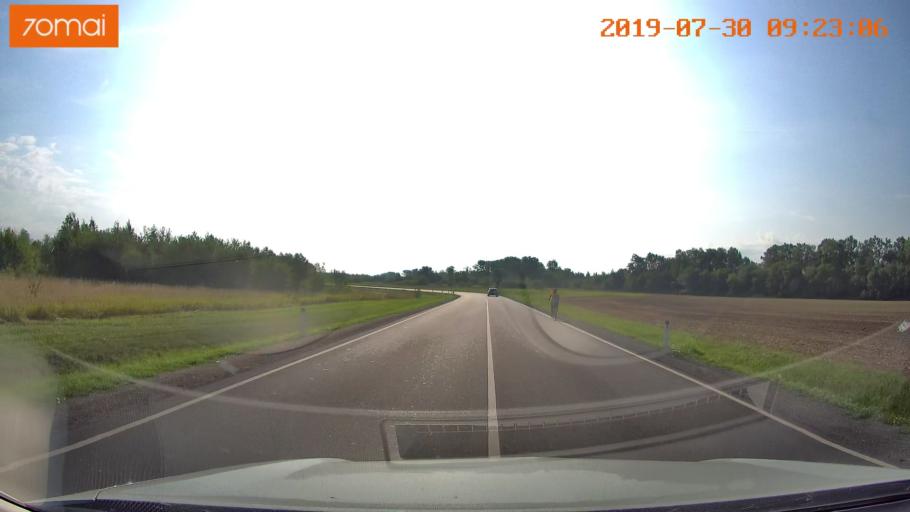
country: LT
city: Kybartai
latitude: 54.6328
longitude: 22.6684
